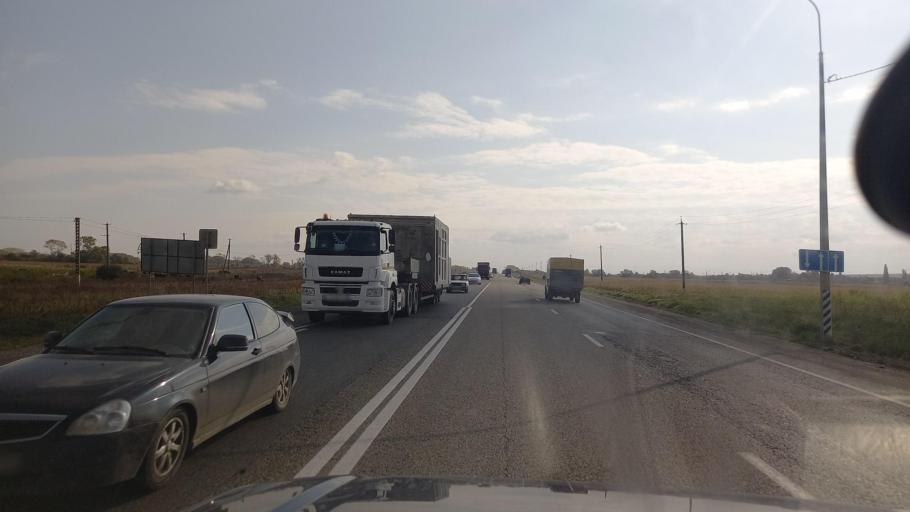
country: RU
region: Krasnodarskiy
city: Novoukrainskiy
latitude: 44.8930
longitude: 38.0656
